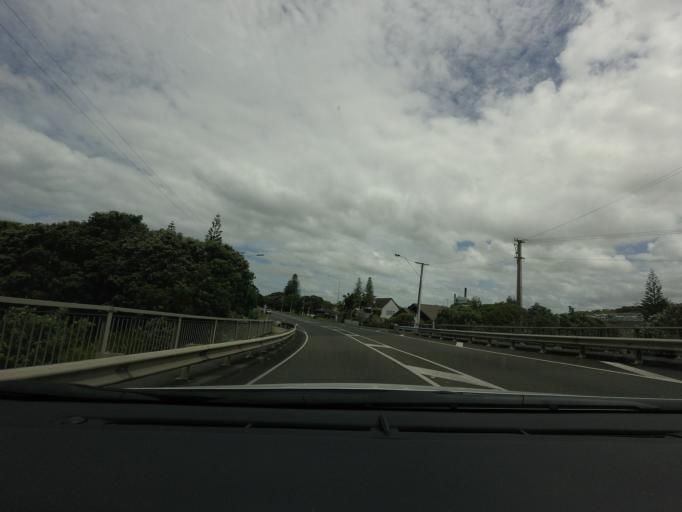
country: NZ
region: Auckland
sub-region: Auckland
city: Rothesay Bay
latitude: -36.5746
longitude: 174.6906
